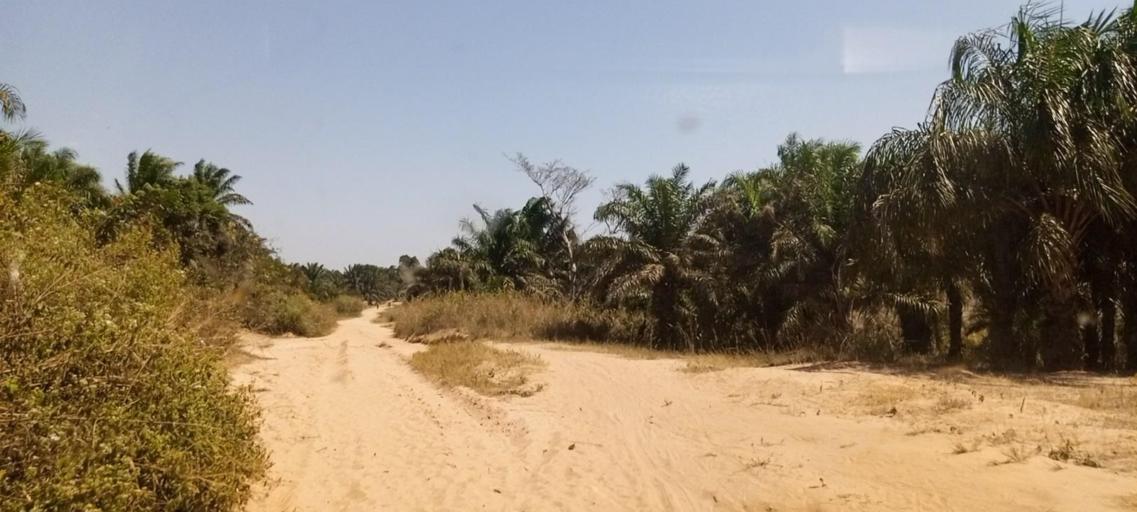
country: CD
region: Kasai-Oriental
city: Kabinda
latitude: -5.9622
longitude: 24.7722
